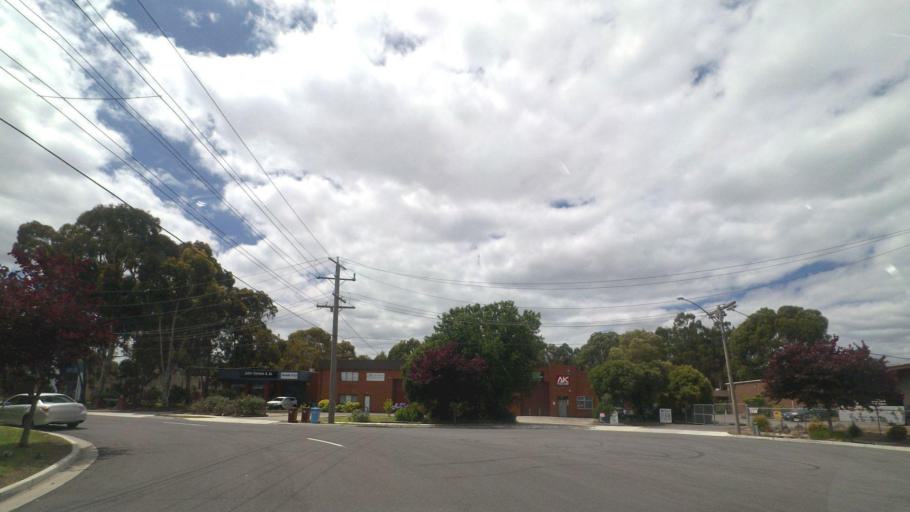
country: AU
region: Victoria
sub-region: Knox
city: Knoxfield
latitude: -37.8705
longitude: 145.2540
